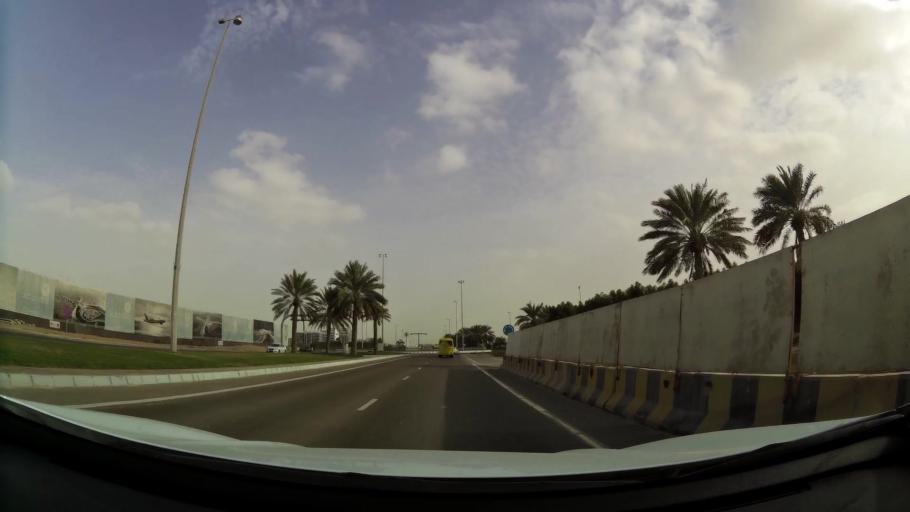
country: AE
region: Abu Dhabi
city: Abu Dhabi
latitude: 24.4313
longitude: 54.6354
